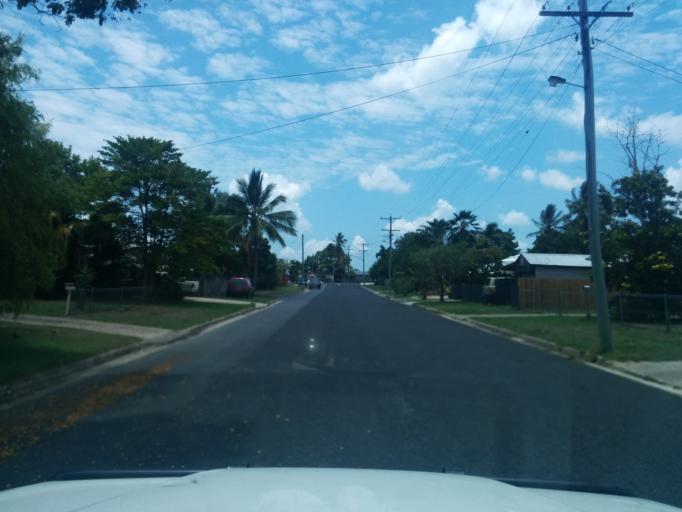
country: AU
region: Queensland
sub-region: Cairns
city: Trinity Beach
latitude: -16.8040
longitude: 145.7004
